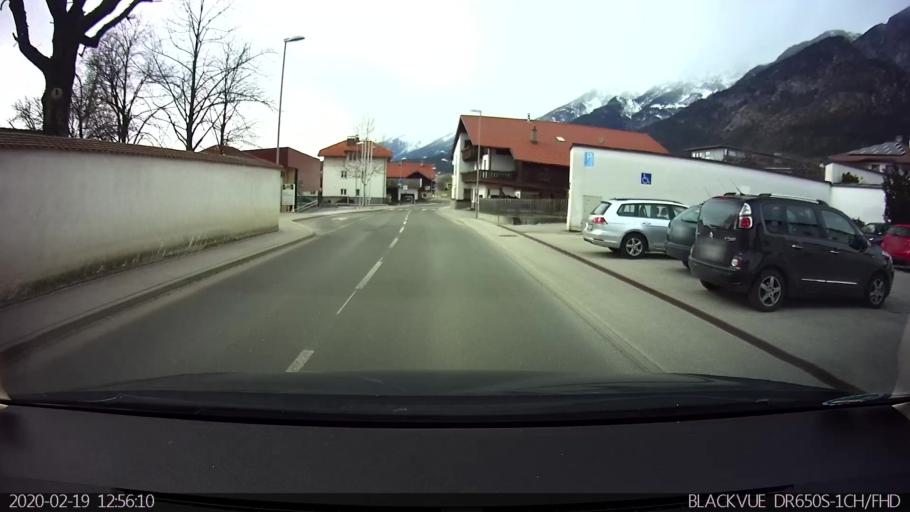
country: AT
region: Tyrol
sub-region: Politischer Bezirk Innsbruck Land
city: Absam
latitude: 47.2959
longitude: 11.5013
